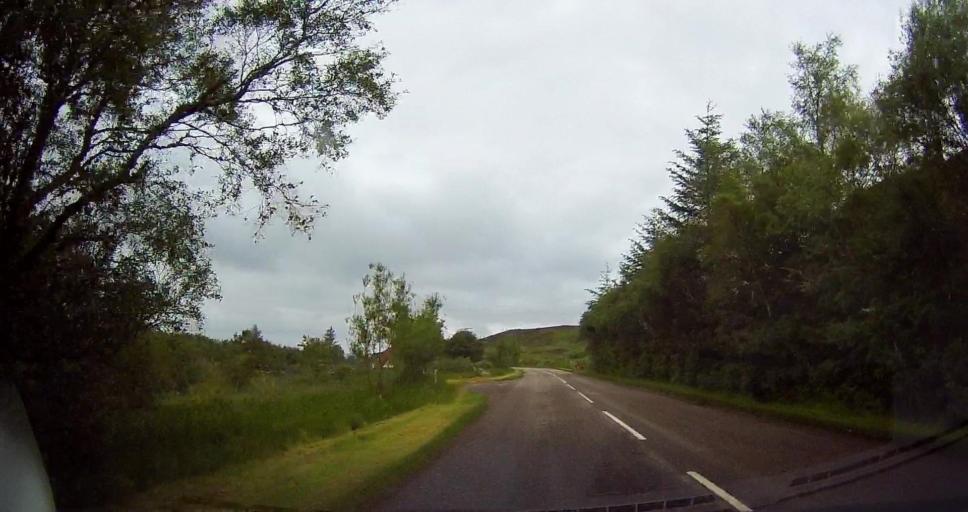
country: GB
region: Scotland
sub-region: Highland
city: Alness
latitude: 58.0188
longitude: -4.3461
